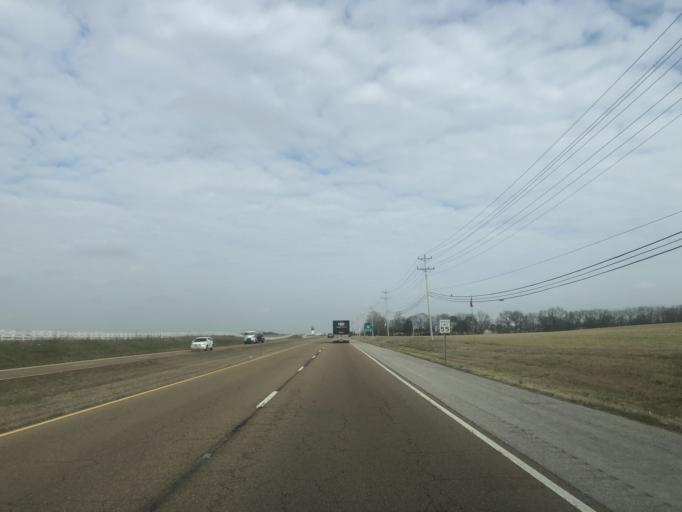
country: US
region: Tennessee
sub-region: Maury County
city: Spring Hill
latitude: 35.7278
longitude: -86.9600
